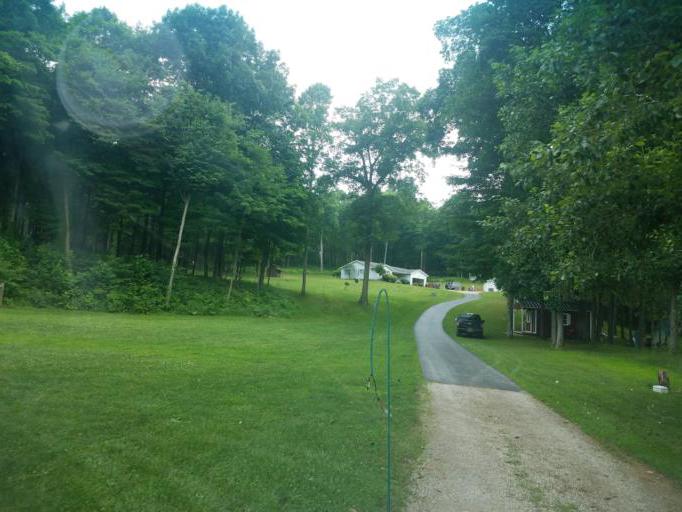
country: US
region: Ohio
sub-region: Sandusky County
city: Bellville
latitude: 40.5548
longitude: -82.4982
